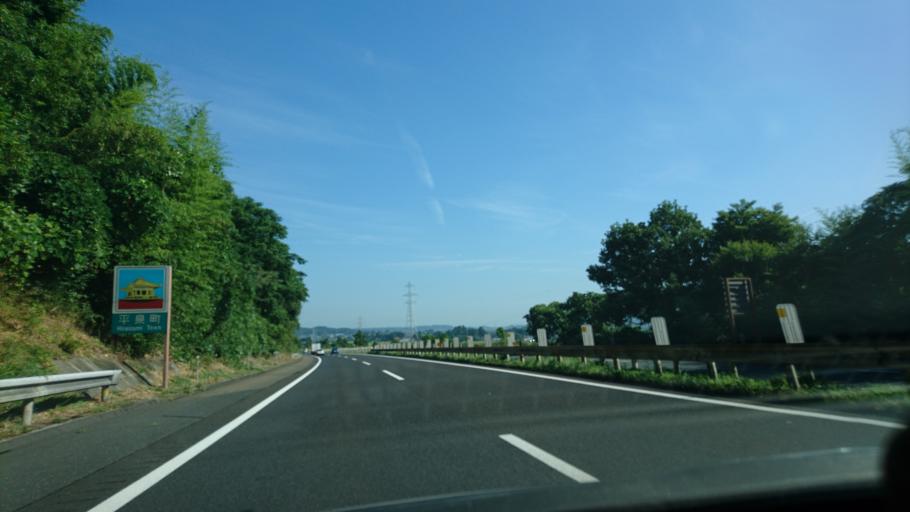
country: JP
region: Iwate
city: Ichinoseki
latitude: 38.9676
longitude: 141.1128
